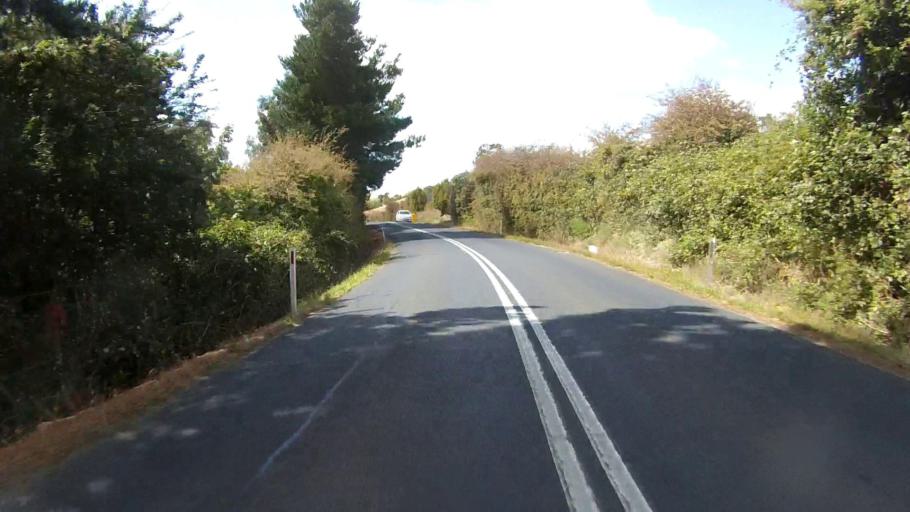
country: AU
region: Tasmania
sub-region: Derwent Valley
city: New Norfolk
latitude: -42.7337
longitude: 146.9111
